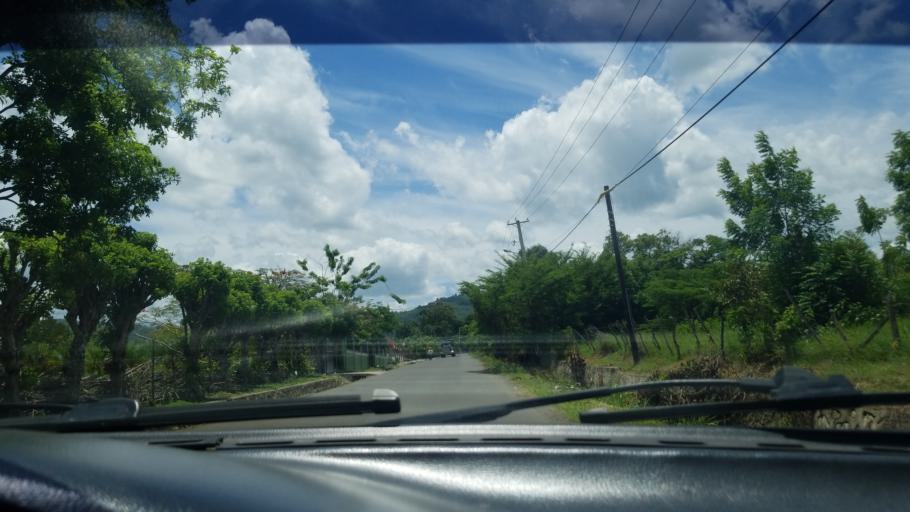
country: DO
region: Santiago
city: Santiago de los Caballeros
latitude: 19.4971
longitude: -70.6757
